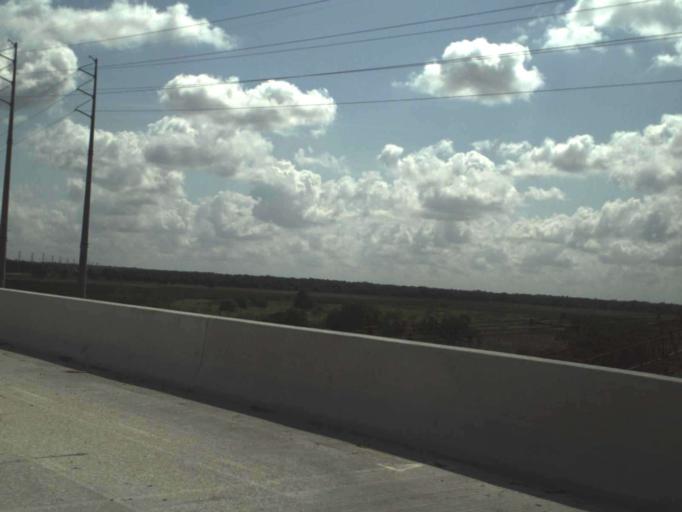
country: US
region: Florida
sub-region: Seminole County
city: Midway
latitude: 28.8021
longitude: -81.2109
